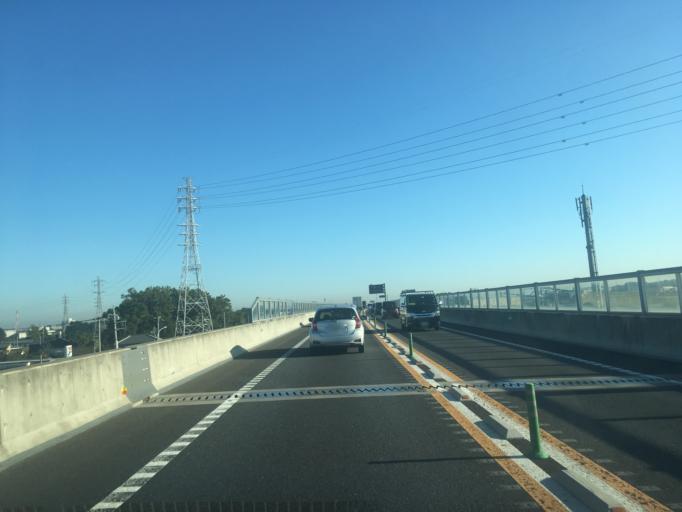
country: JP
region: Saitama
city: Kukichuo
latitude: 36.0518
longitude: 139.6873
